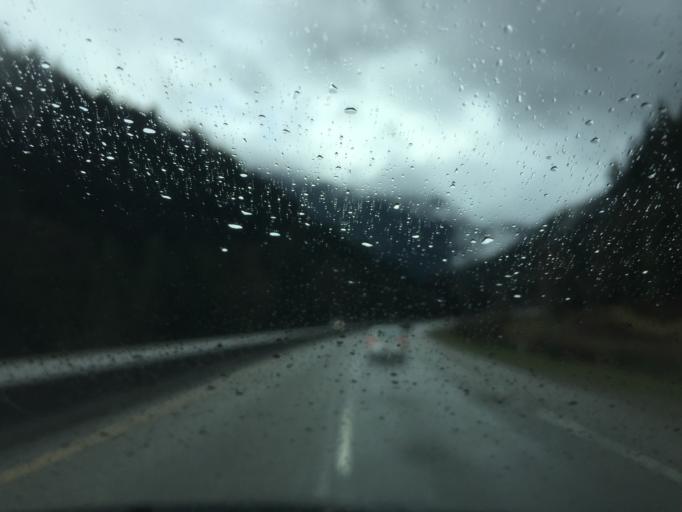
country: CA
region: British Columbia
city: Hope
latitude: 49.4020
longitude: -121.3158
